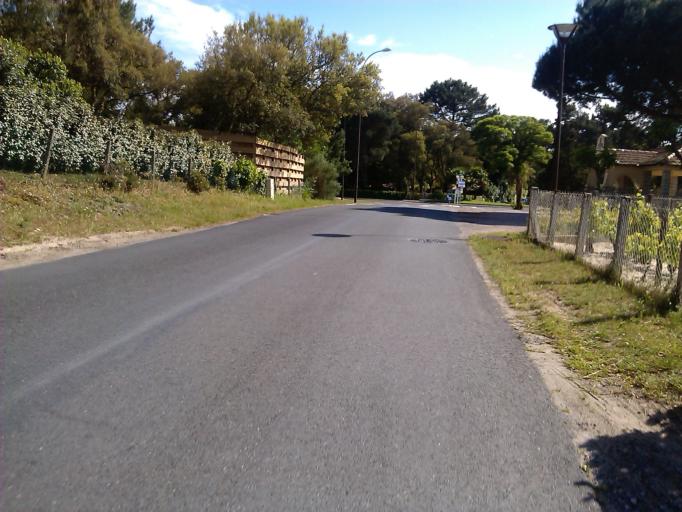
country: FR
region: Aquitaine
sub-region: Departement des Landes
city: Leon
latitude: 43.8522
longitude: -1.3594
